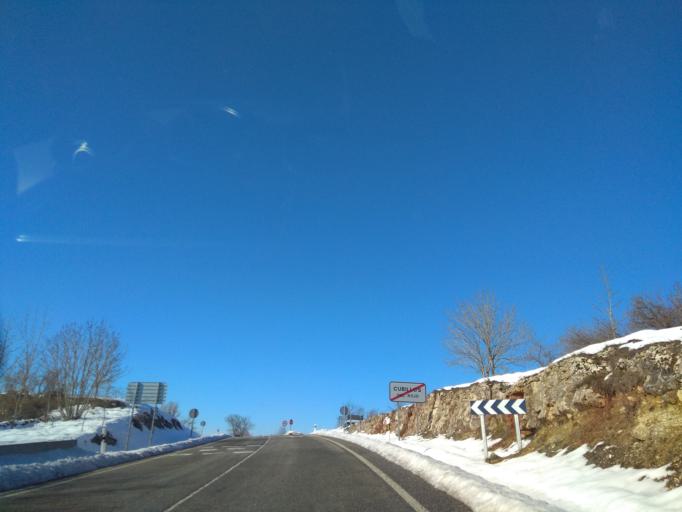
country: ES
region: Cantabria
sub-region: Provincia de Cantabria
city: San Martin de Elines
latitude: 42.9356
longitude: -3.7185
